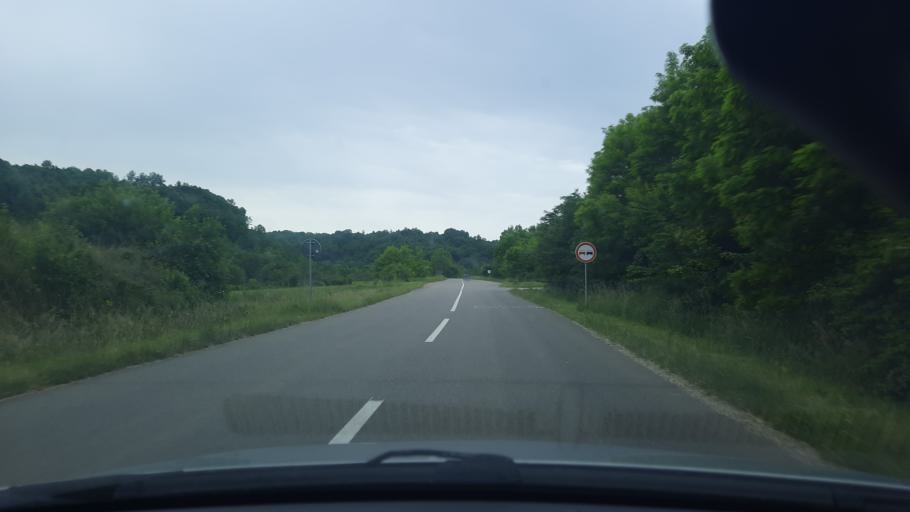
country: RS
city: Bukor
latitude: 44.5202
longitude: 19.5124
